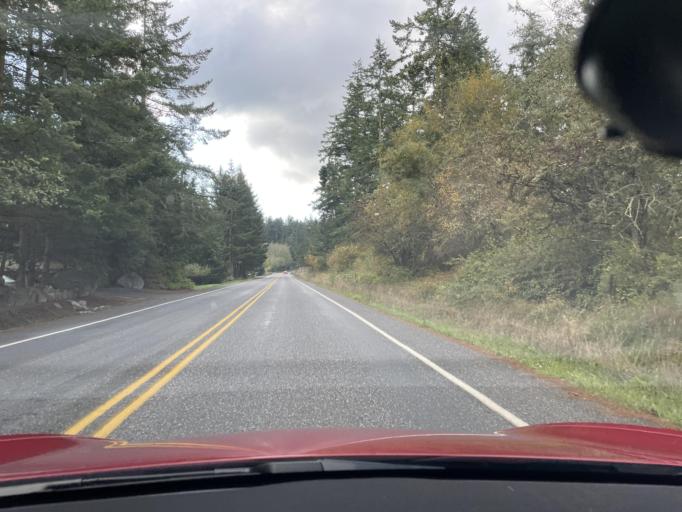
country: US
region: Washington
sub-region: San Juan County
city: Friday Harbor
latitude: 48.5002
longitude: -123.0344
